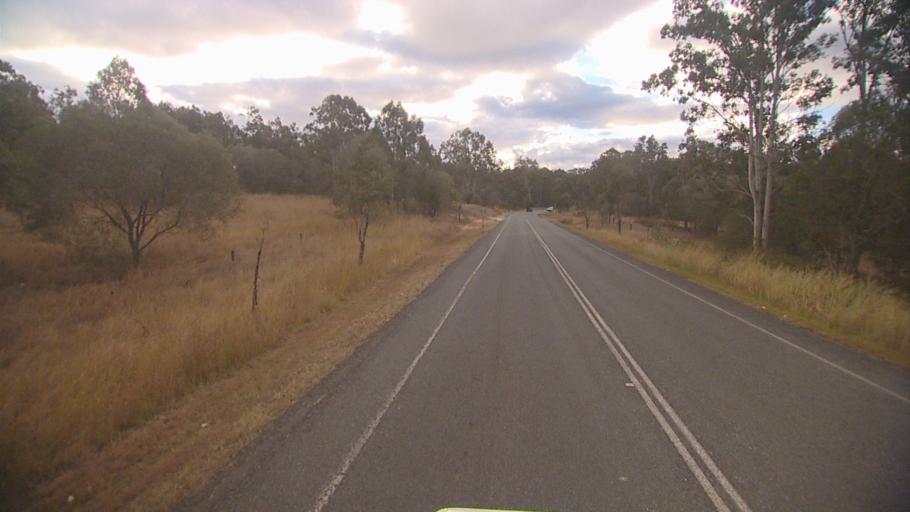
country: AU
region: Queensland
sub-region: Logan
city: Cedar Vale
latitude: -27.9106
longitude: 153.0910
